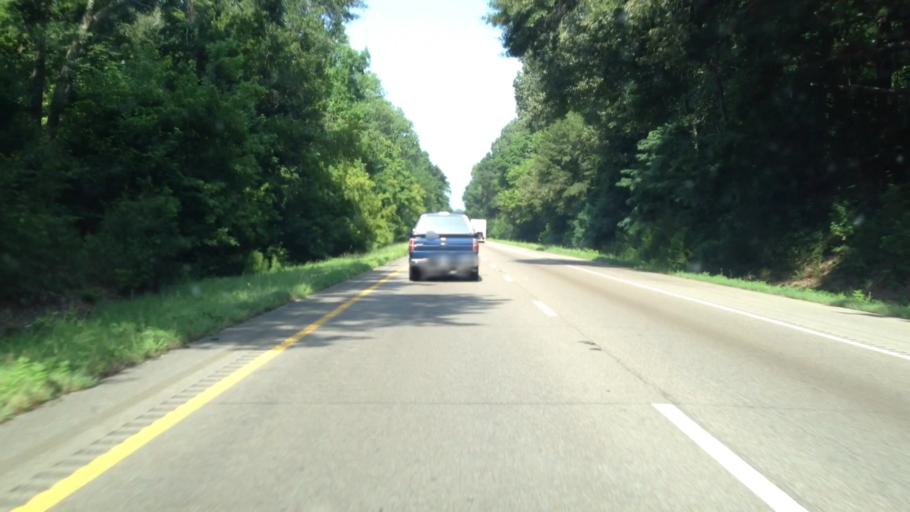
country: US
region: Mississippi
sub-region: Warren County
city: Beechwood
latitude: 32.3532
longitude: -90.7911
